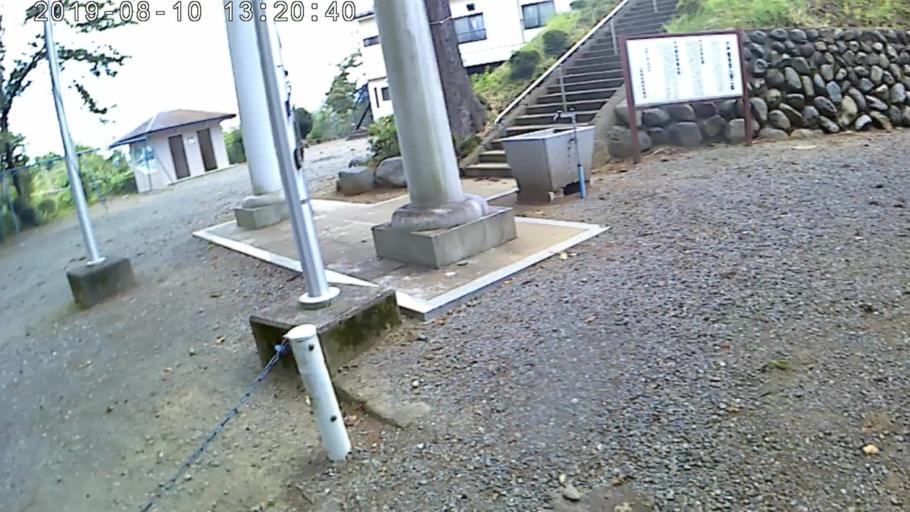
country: JP
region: Yamanashi
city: Uenohara
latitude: 35.6306
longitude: 139.0836
